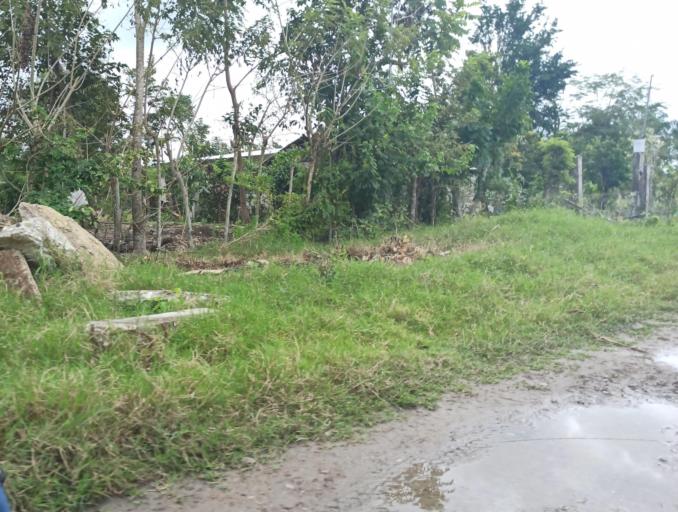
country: MX
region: Puebla
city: Espinal
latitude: 20.3241
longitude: -97.4194
